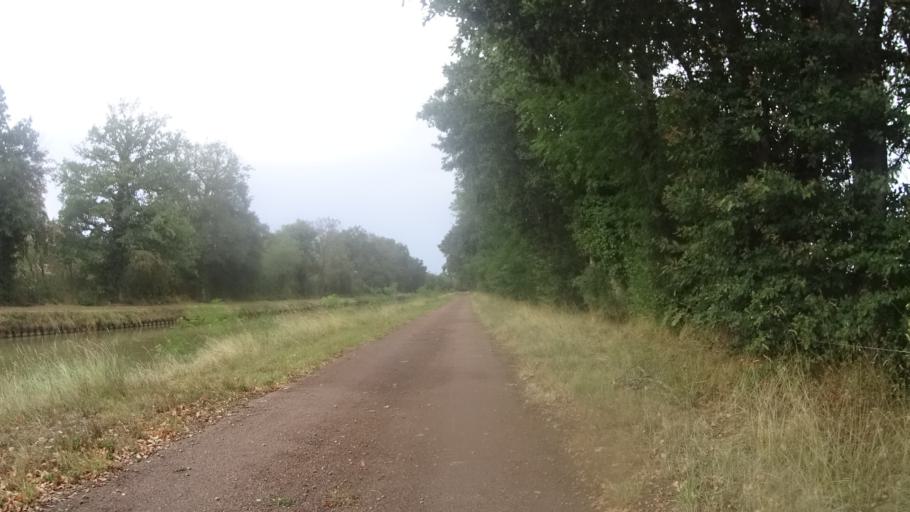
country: FR
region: Bourgogne
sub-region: Departement de la Nievre
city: Imphy
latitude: 46.8975
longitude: 3.2458
